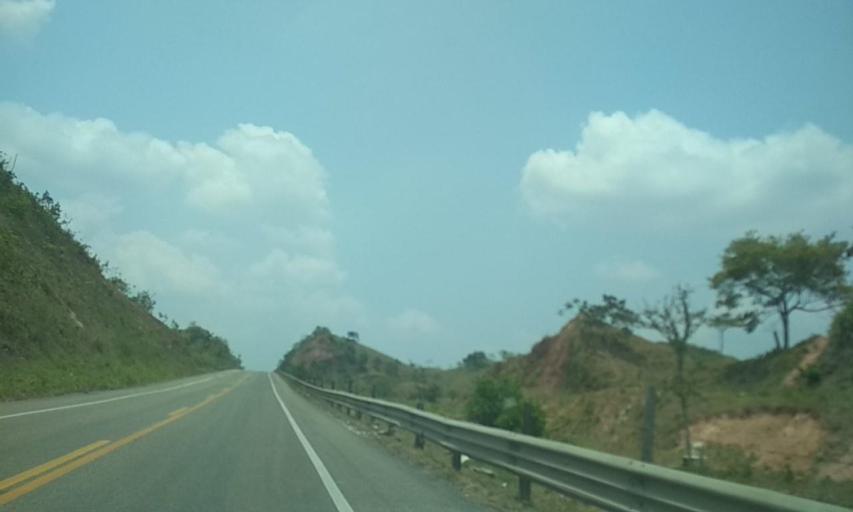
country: MX
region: Tabasco
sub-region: Huimanguillo
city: Francisco Rueda
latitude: 17.6552
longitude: -93.8448
